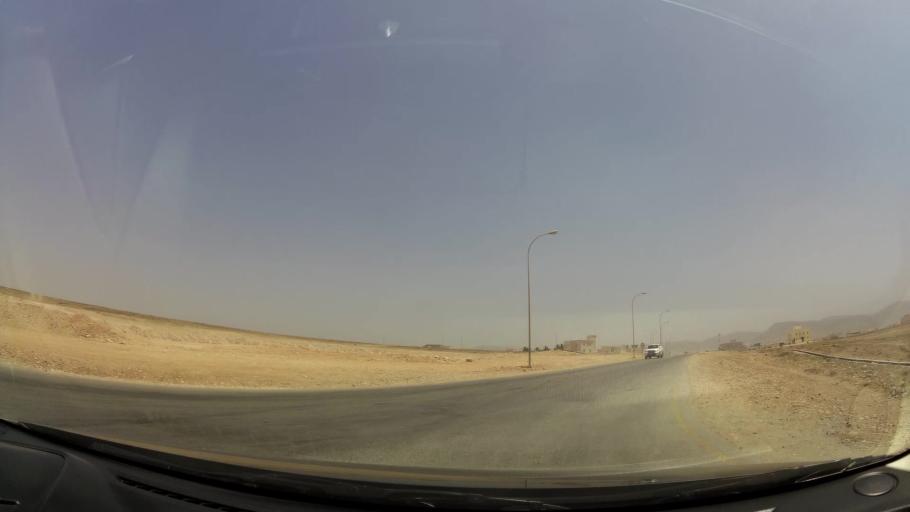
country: OM
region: Zufar
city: Salalah
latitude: 17.0822
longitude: 54.1891
